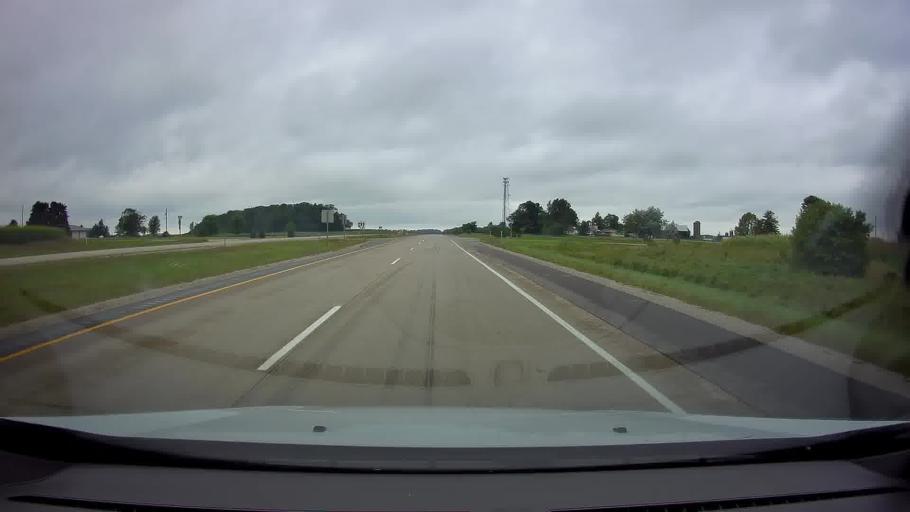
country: US
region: Wisconsin
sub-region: Brown County
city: Pulaski
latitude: 44.6435
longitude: -88.2913
